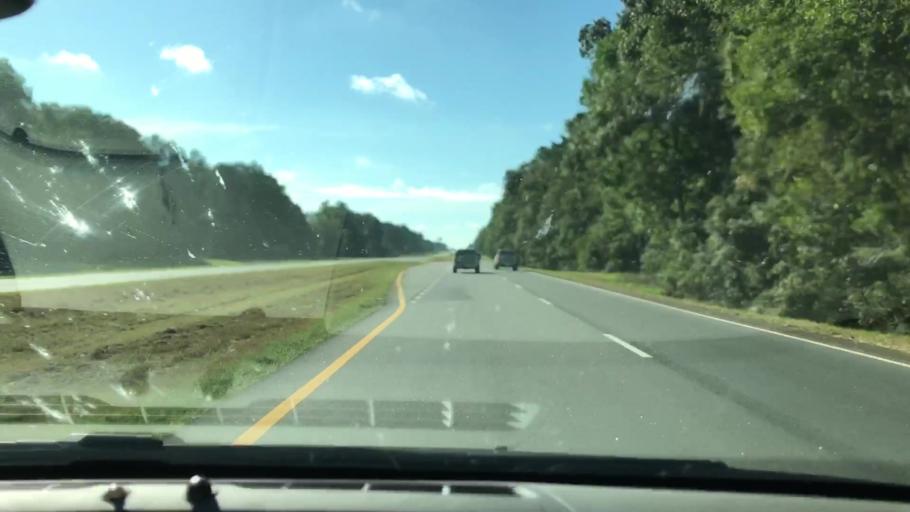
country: US
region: Georgia
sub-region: Lee County
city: Leesburg
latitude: 31.6565
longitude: -84.2712
